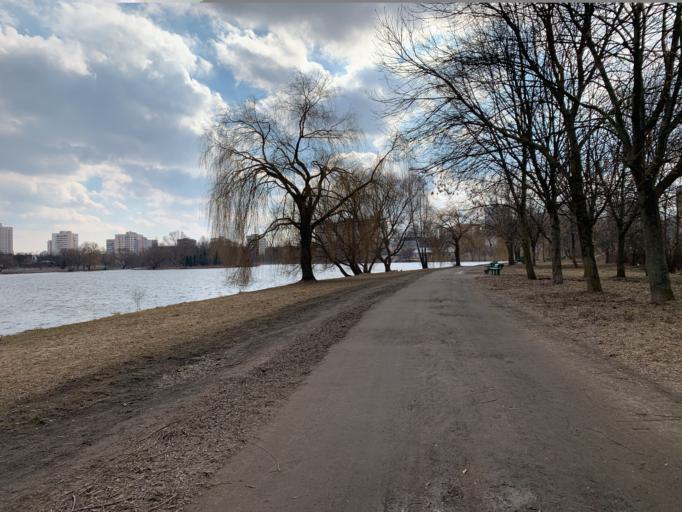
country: BY
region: Minsk
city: Minsk
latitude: 53.8800
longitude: 27.5712
